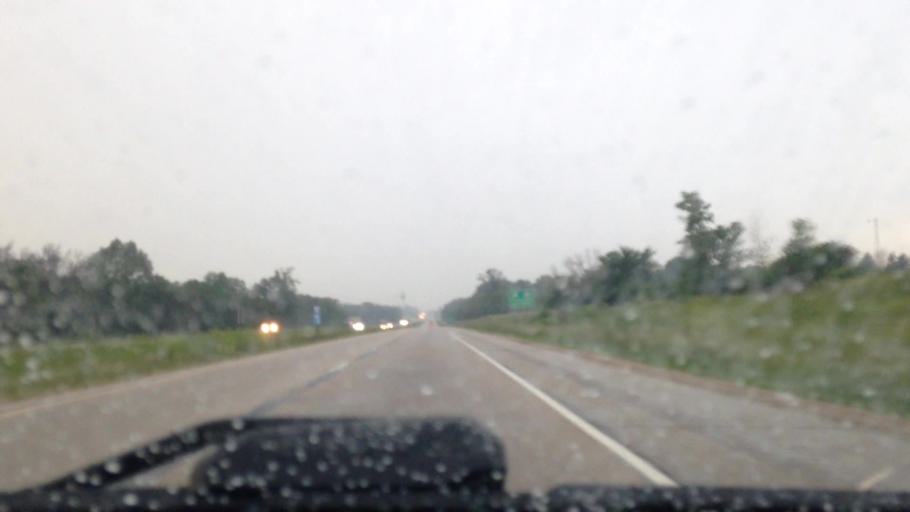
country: US
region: Wisconsin
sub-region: Washington County
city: Slinger
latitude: 43.4079
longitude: -88.3274
